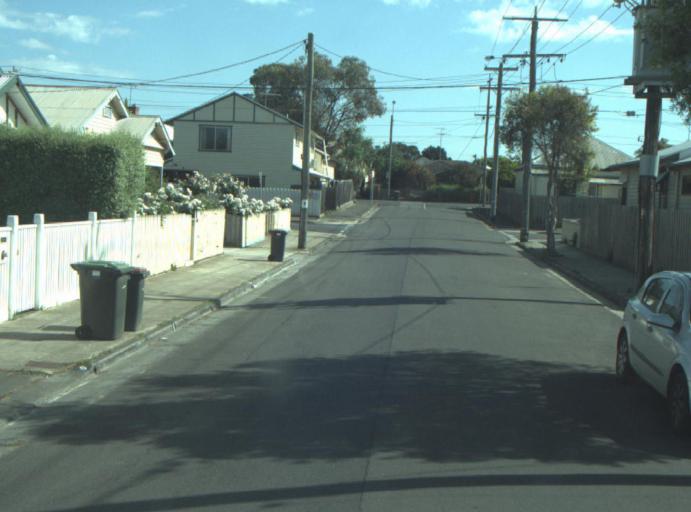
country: AU
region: Victoria
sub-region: Greater Geelong
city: Geelong West
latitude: -38.1429
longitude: 144.3389
